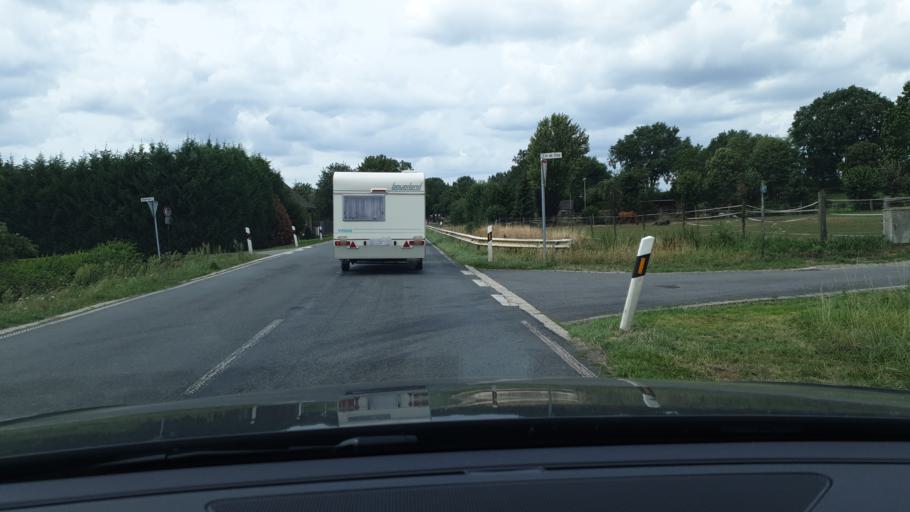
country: DE
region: North Rhine-Westphalia
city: Straelen
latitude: 51.4288
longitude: 6.2431
